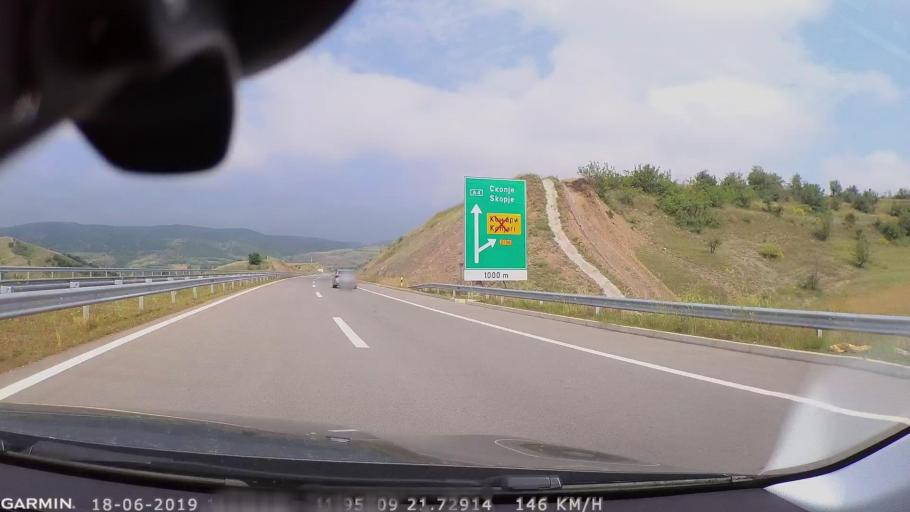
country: MK
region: Sveti Nikole
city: Gorobinci
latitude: 41.9306
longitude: 21.8281
